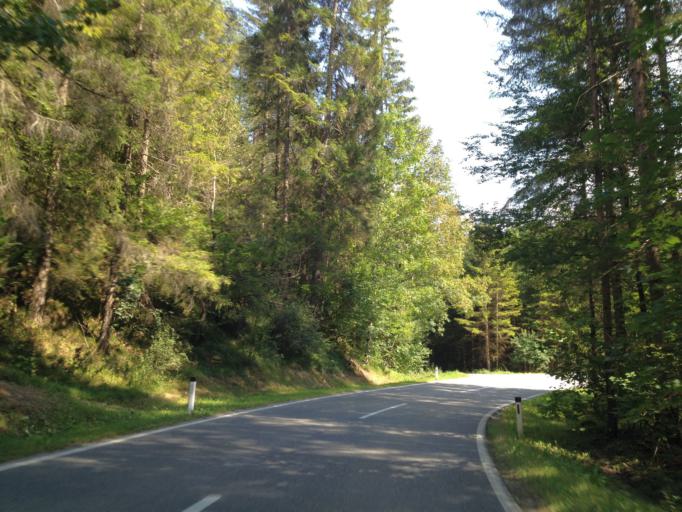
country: AT
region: Styria
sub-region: Politischer Bezirk Liezen
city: Haus
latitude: 47.4194
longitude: 13.7290
